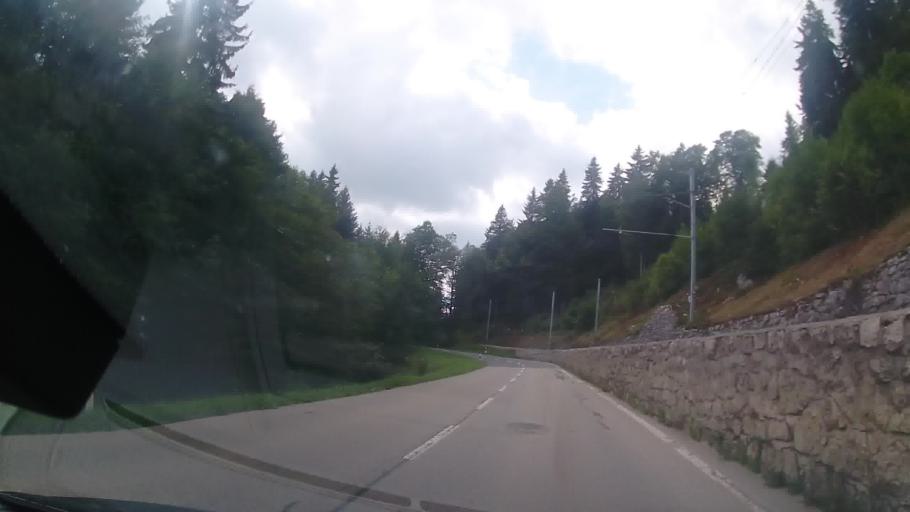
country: CH
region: Vaud
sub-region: Nyon District
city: Saint-Cergue
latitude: 46.4481
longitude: 6.1405
